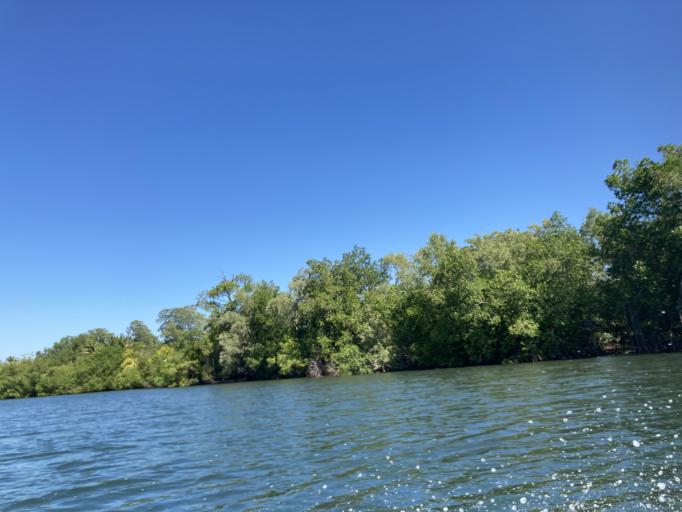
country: GT
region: Jutiapa
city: Pasaco
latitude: 13.8060
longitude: -90.2695
